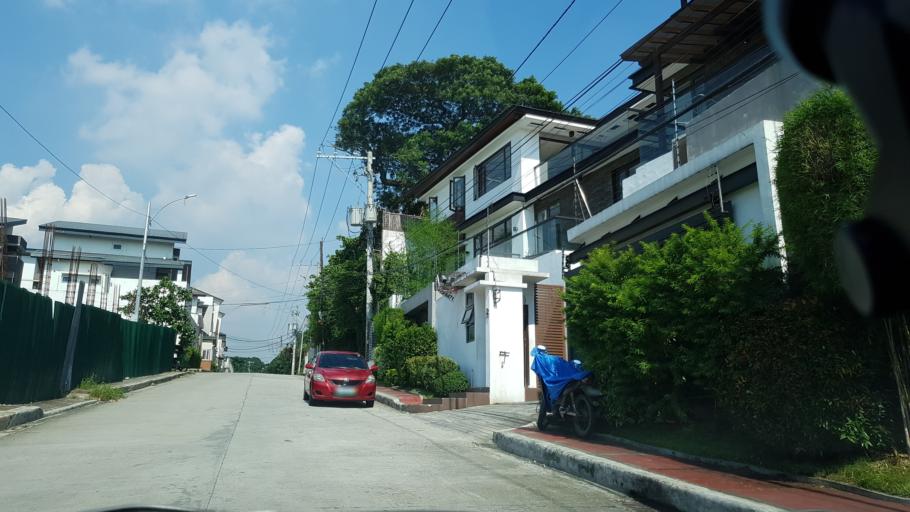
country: PH
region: Metro Manila
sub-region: San Juan
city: San Juan
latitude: 14.6150
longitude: 121.0287
